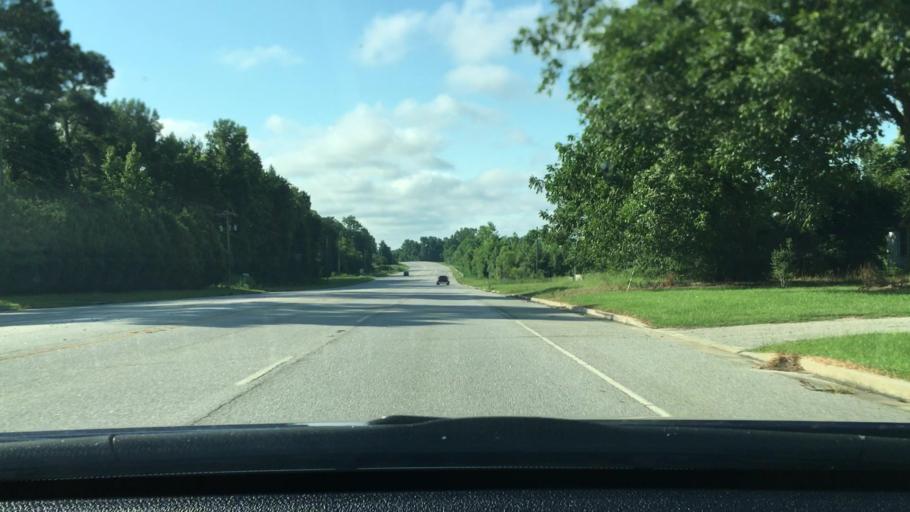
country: US
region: South Carolina
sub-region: Clarendon County
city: Manning
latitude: 33.7540
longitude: -80.2235
